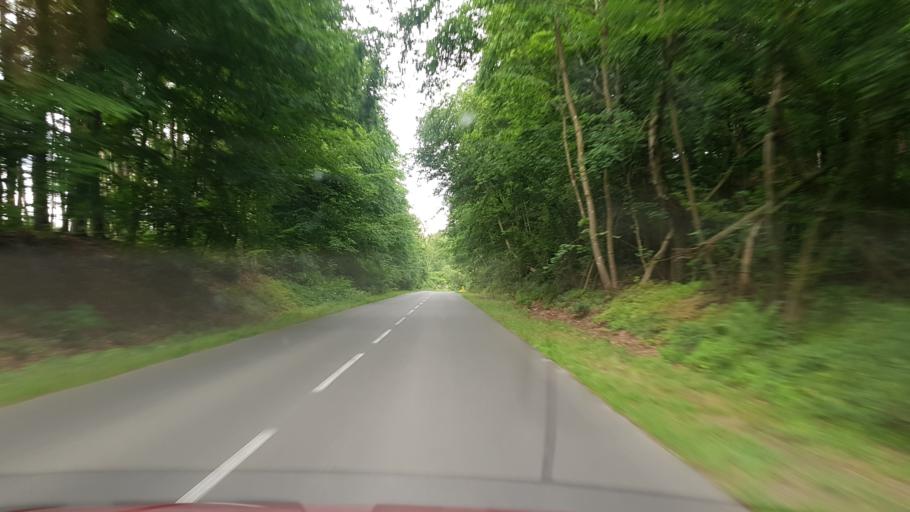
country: PL
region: West Pomeranian Voivodeship
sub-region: Powiat gryficki
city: Gryfice
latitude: 53.8523
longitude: 15.1105
